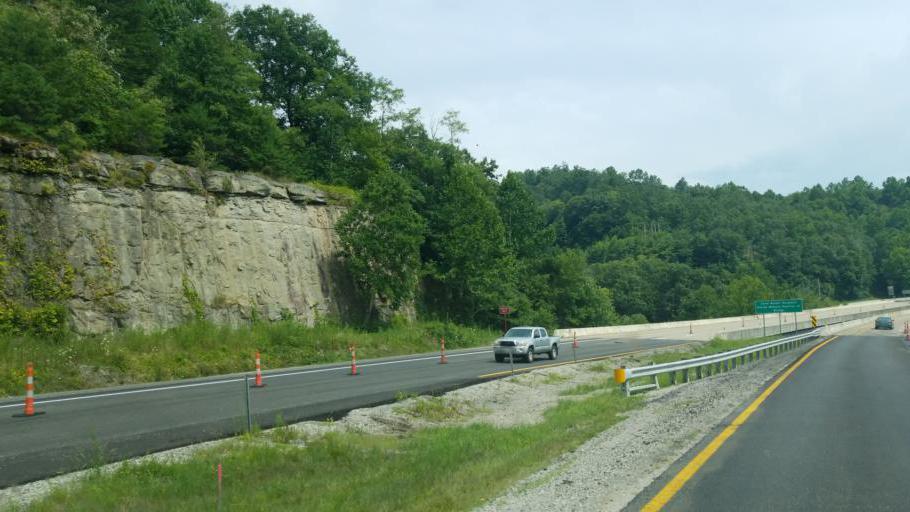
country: US
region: West Virginia
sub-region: Kanawha County
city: Alum Creek
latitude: 38.2238
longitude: -81.8355
